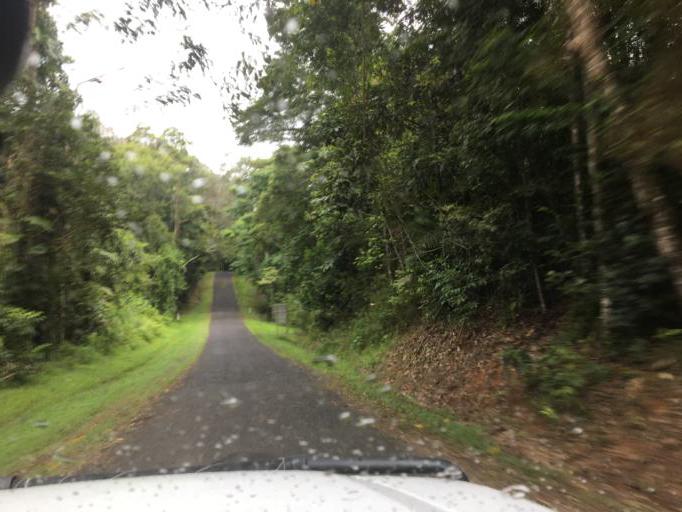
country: AU
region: Queensland
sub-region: Tablelands
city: Kuranda
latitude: -16.8437
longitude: 145.6430
